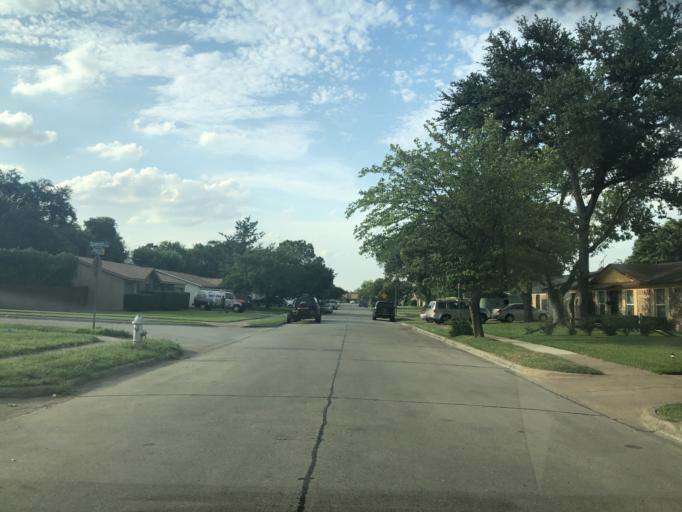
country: US
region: Texas
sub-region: Dallas County
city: Irving
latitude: 32.7861
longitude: -96.9683
